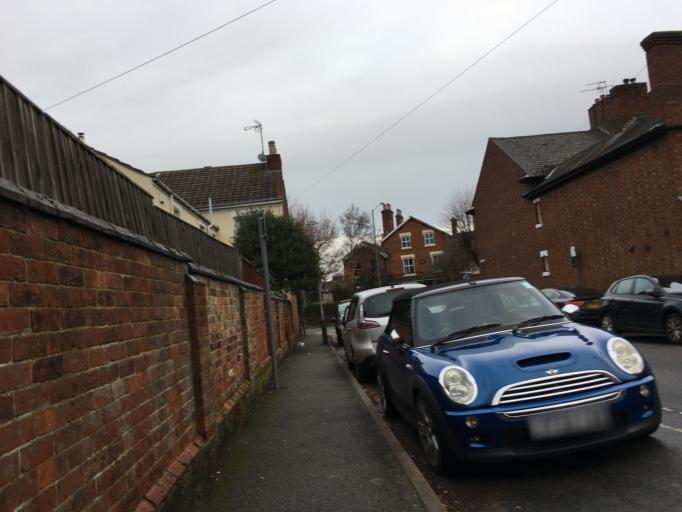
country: GB
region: England
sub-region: Warwickshire
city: Rugby
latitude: 52.3719
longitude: -1.2504
